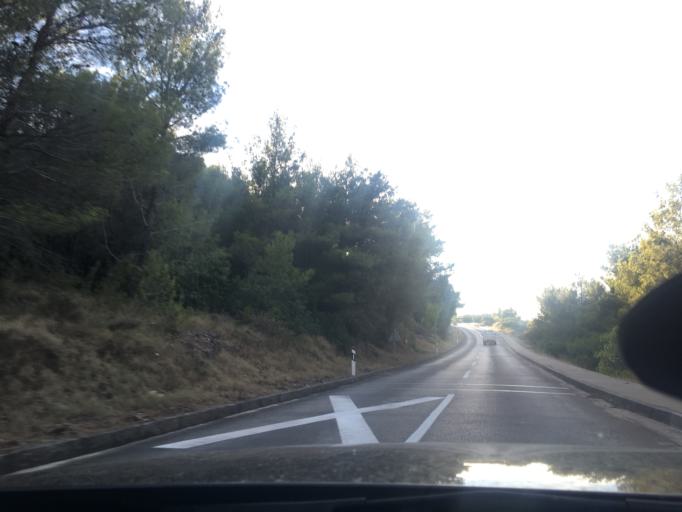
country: HR
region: Splitsko-Dalmatinska
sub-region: Grad Vis
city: Vis
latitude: 43.0565
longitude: 16.1924
